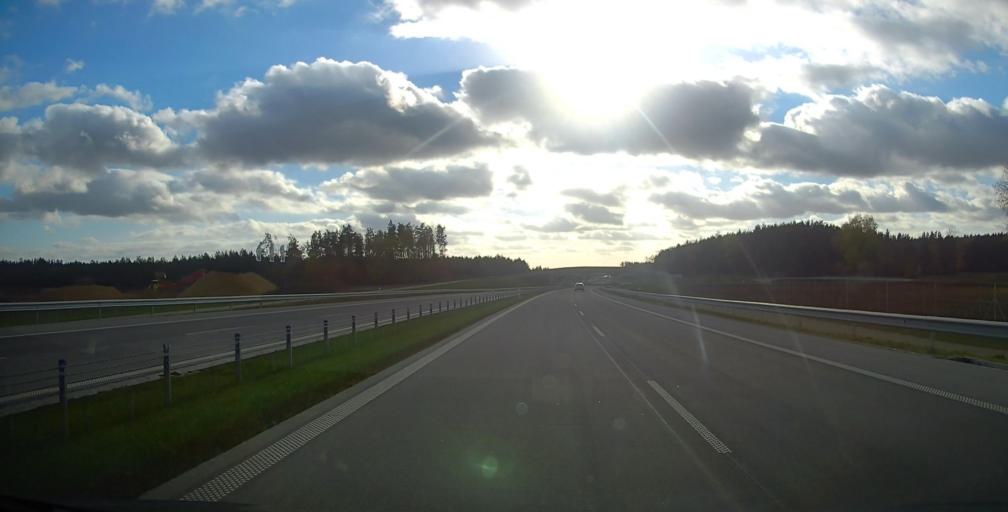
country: PL
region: Podlasie
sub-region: Powiat kolnenski
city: Stawiski
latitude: 53.2892
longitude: 22.1448
